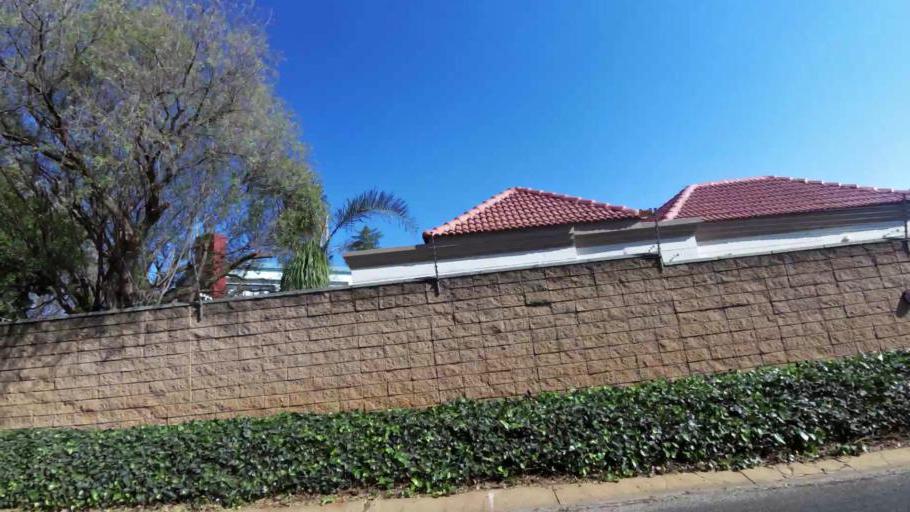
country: ZA
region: Gauteng
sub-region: City of Johannesburg Metropolitan Municipality
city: Roodepoort
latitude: -26.1334
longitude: 27.9611
